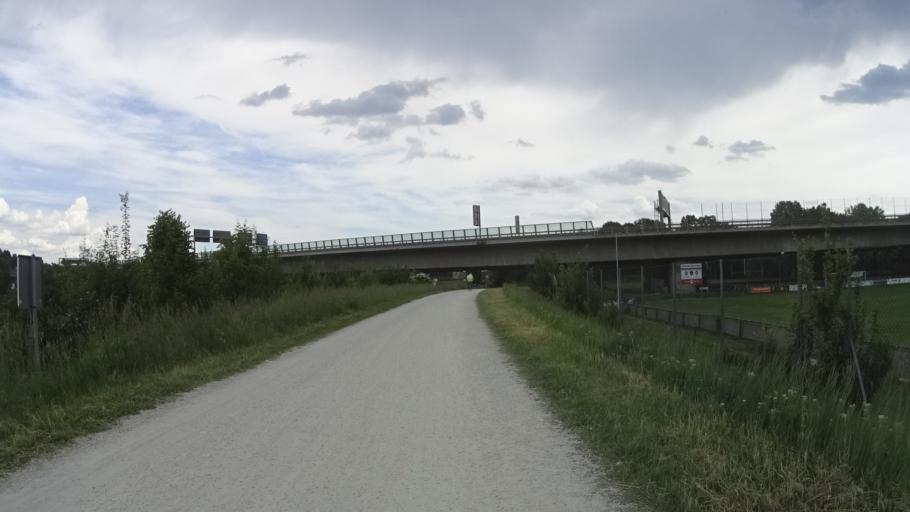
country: DE
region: Bavaria
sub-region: Upper Palatinate
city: Lappersdorf
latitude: 49.0287
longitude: 12.0735
